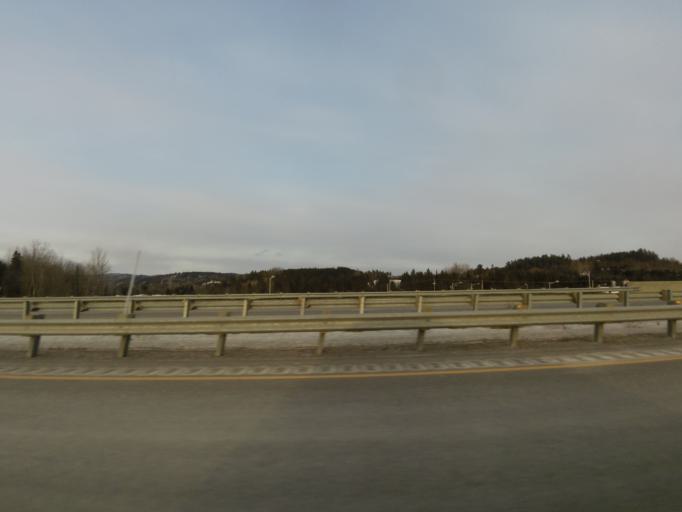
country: CA
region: Quebec
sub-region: Outaouais
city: Wakefield
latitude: 45.6273
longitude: -75.9371
